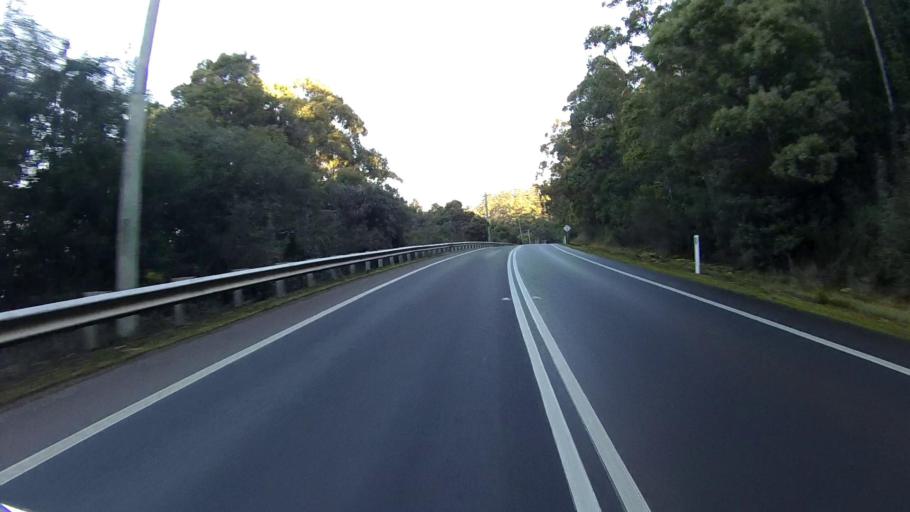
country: AU
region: Tasmania
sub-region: Clarence
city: Sandford
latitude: -43.1162
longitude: 147.8546
